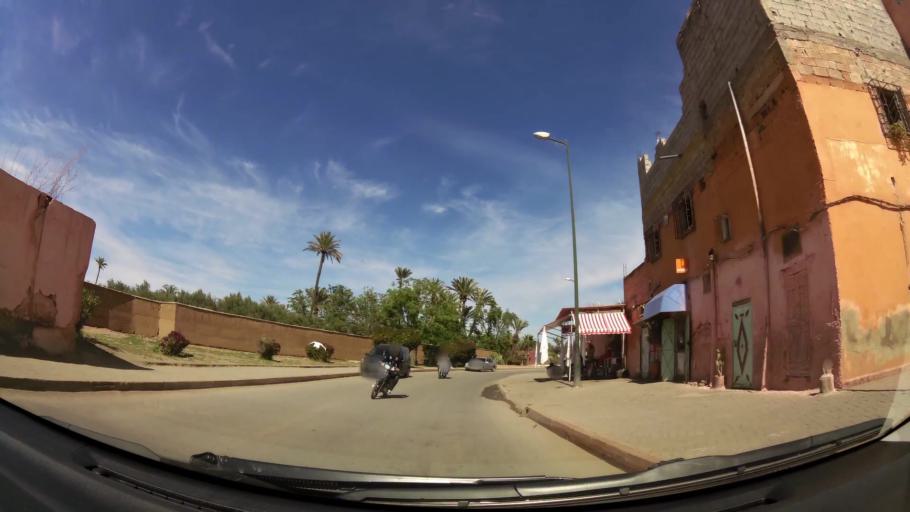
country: MA
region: Marrakech-Tensift-Al Haouz
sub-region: Marrakech
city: Marrakesh
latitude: 31.6252
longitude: -7.9652
